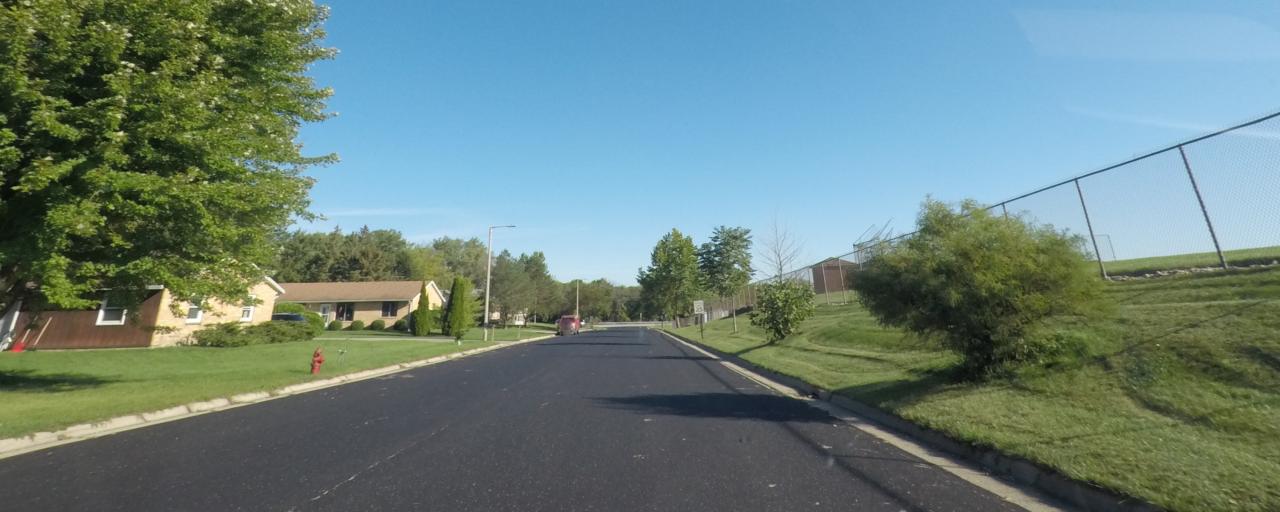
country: US
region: Wisconsin
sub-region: Jefferson County
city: Cambridge
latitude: 43.0066
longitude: -89.0120
